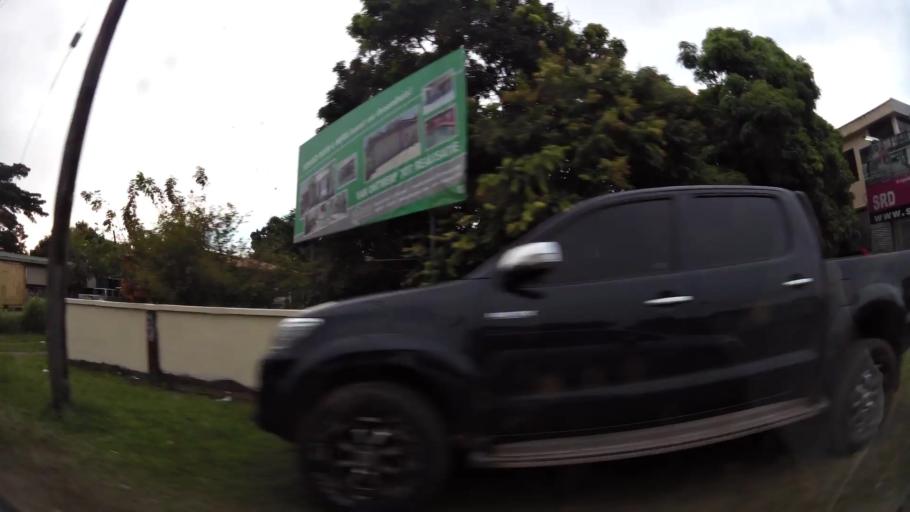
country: SR
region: Paramaribo
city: Paramaribo
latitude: 5.8284
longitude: -55.1976
